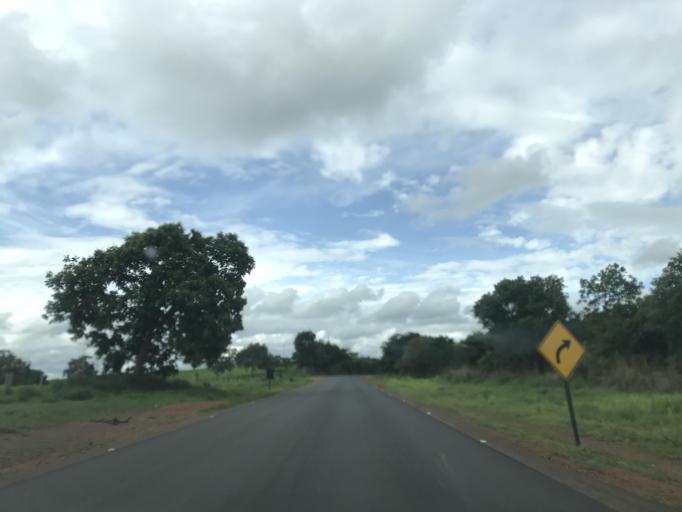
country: BR
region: Goias
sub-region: Bela Vista De Goias
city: Bela Vista de Goias
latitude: -17.0417
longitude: -48.6632
